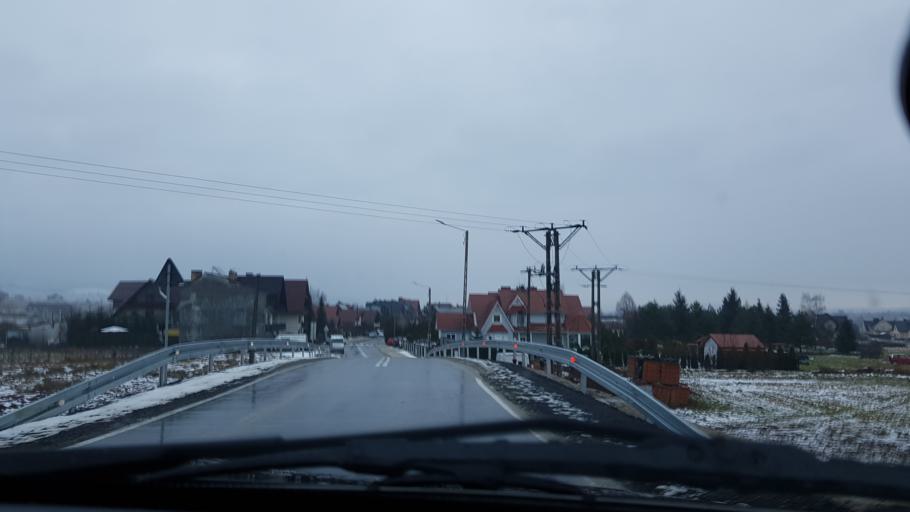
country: PL
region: Lesser Poland Voivodeship
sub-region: Powiat nowotarski
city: Ludzmierz
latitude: 49.4855
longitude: 19.9957
